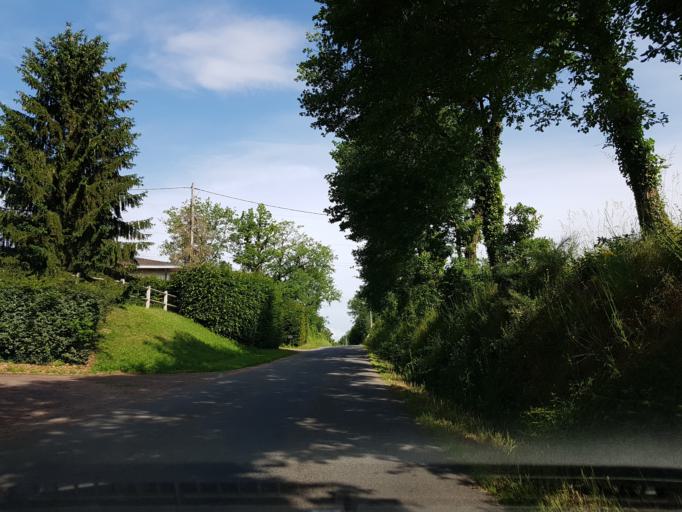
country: FR
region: Poitou-Charentes
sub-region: Departement de la Charente
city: Chabanais
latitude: 45.8817
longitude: 0.7101
